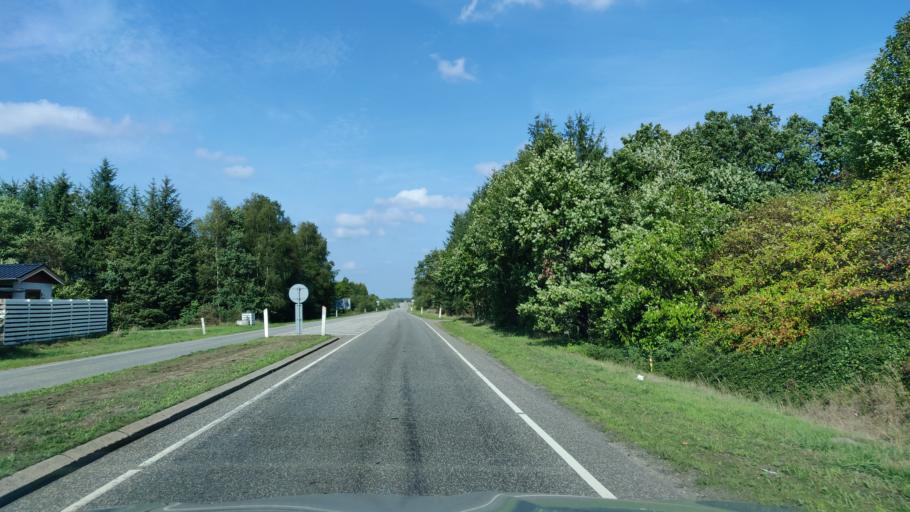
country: DK
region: Central Jutland
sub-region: Herning Kommune
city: Sunds
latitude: 56.3323
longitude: 8.9848
